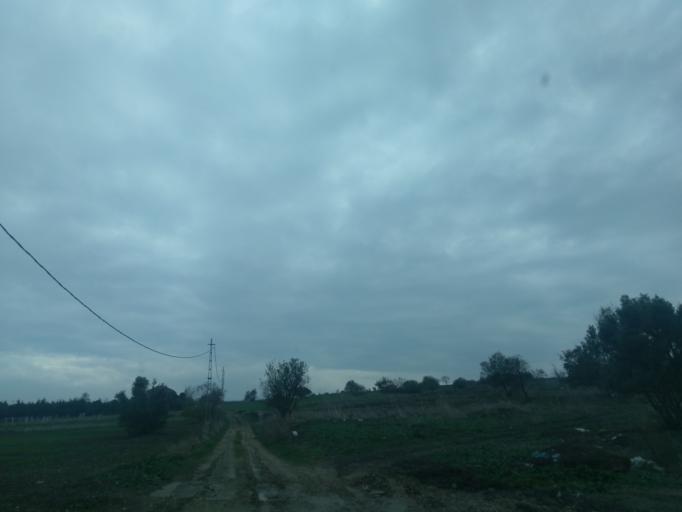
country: TR
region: Istanbul
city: Canta
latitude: 41.1035
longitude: 28.0788
